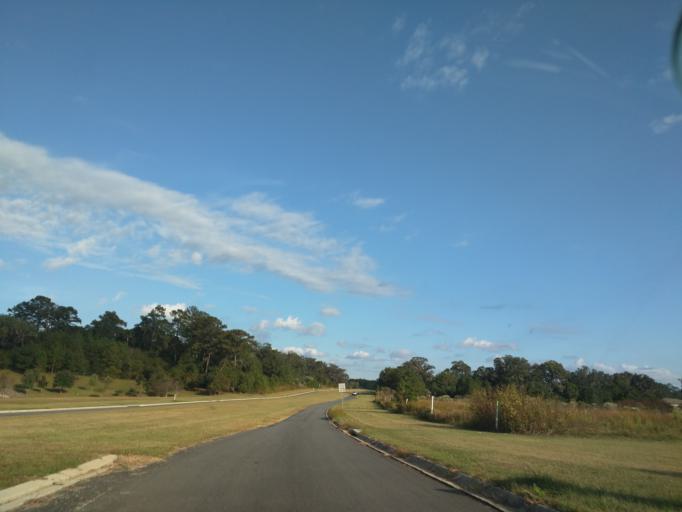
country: US
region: Florida
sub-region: Leon County
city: Tallahassee
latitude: 30.4121
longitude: -84.2184
